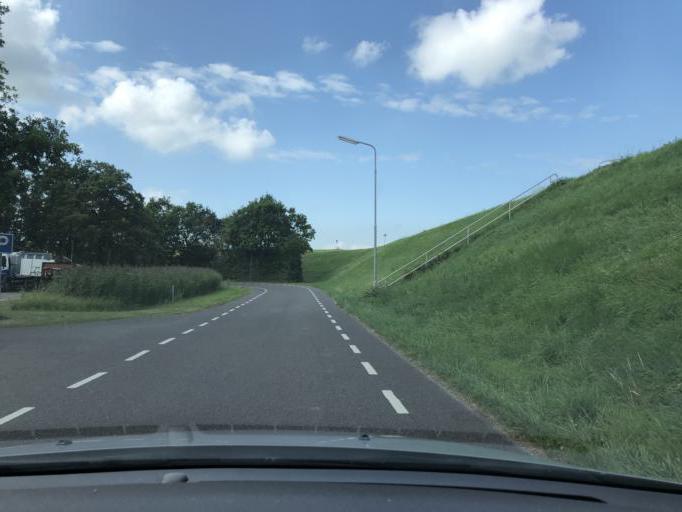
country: NL
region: Zeeland
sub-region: Gemeente Reimerswaal
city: Yerseke
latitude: 51.5021
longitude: 4.0521
